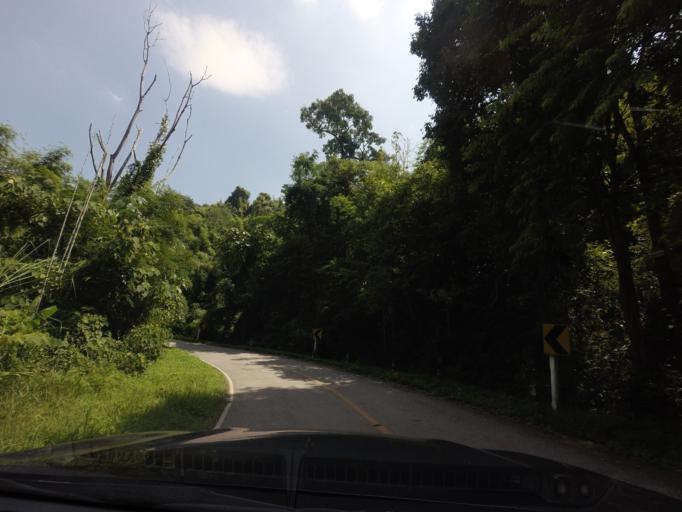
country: TH
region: Loei
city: Na Haeo
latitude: 17.6223
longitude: 100.9007
